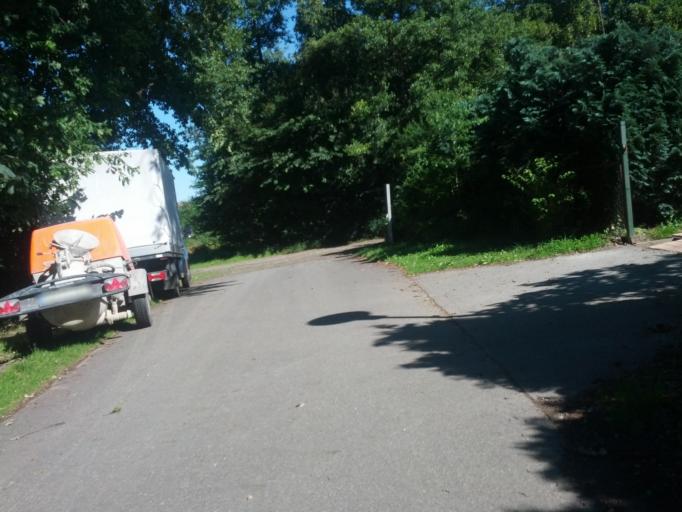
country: DE
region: Mecklenburg-Vorpommern
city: Bastorf
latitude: 54.1156
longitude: 11.6752
